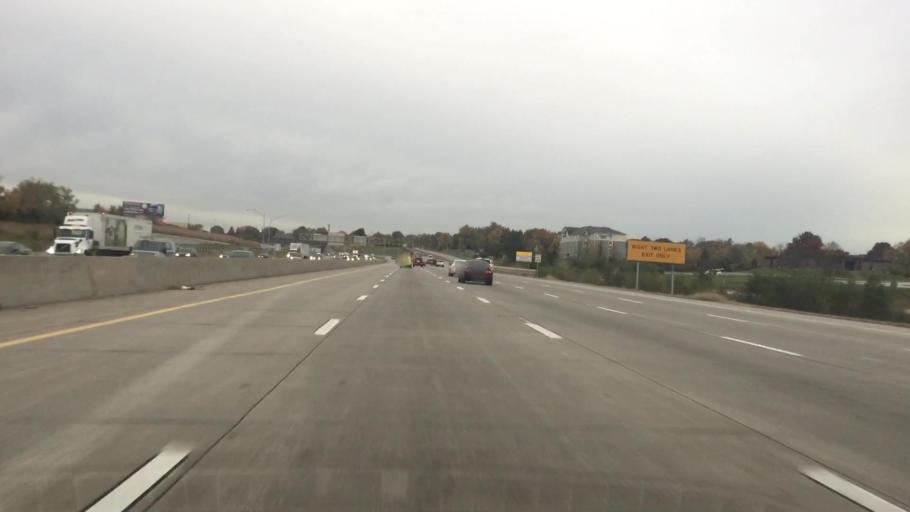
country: US
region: Missouri
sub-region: Jackson County
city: Grandview
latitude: 38.9232
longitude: -94.5278
